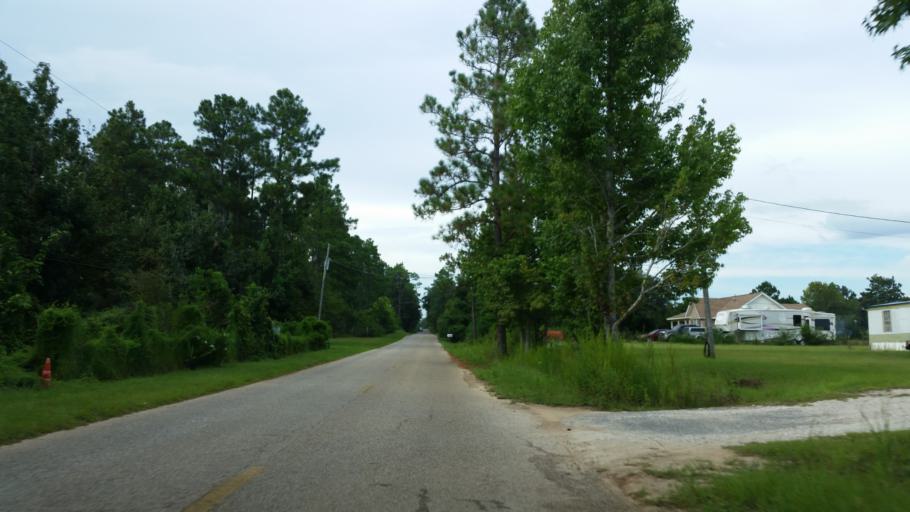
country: US
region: Florida
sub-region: Santa Rosa County
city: Point Baker
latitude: 30.7048
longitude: -86.9558
